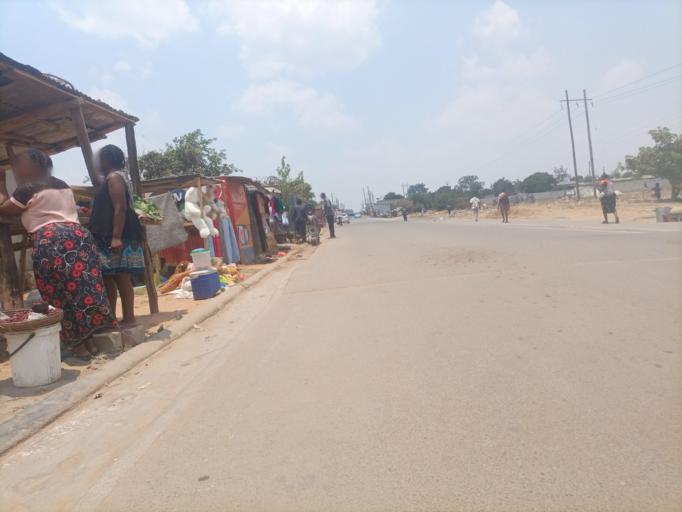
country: ZM
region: Lusaka
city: Lusaka
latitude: -15.4032
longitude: 28.3695
